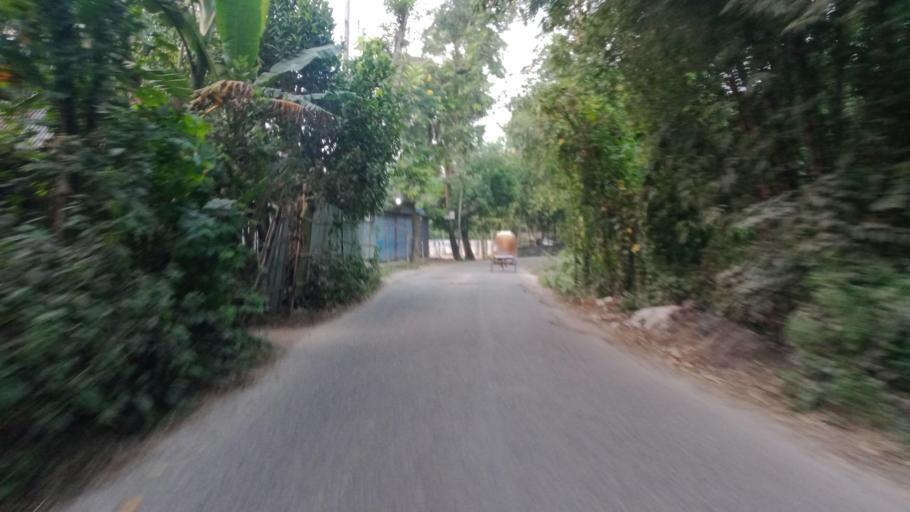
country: BD
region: Chittagong
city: Hajiganj
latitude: 23.3752
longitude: 90.9837
